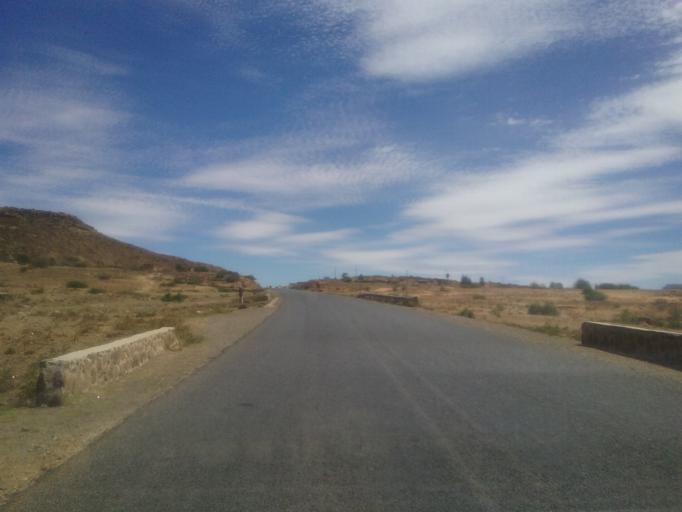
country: LS
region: Mohale's Hoek District
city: Mohale's Hoek
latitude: -30.0718
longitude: 27.4242
